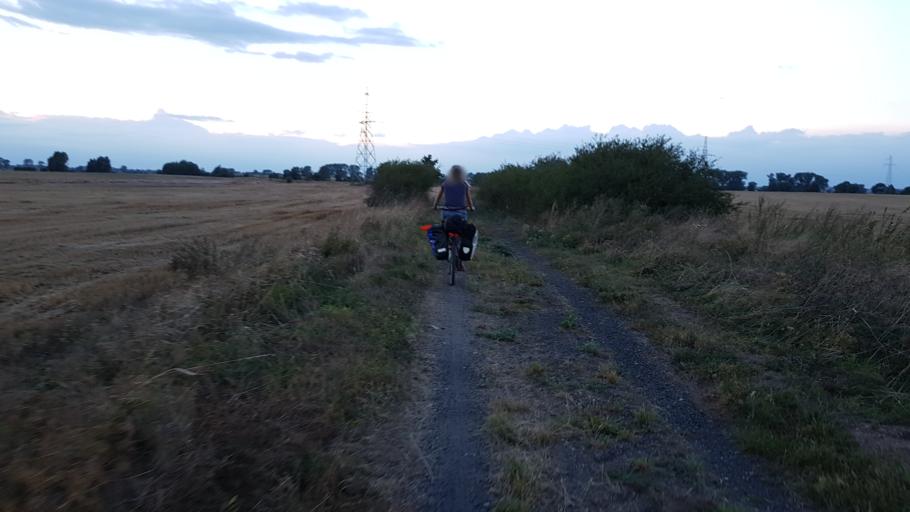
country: PL
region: West Pomeranian Voivodeship
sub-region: Powiat pyrzycki
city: Przelewice
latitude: 53.1296
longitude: 15.0425
